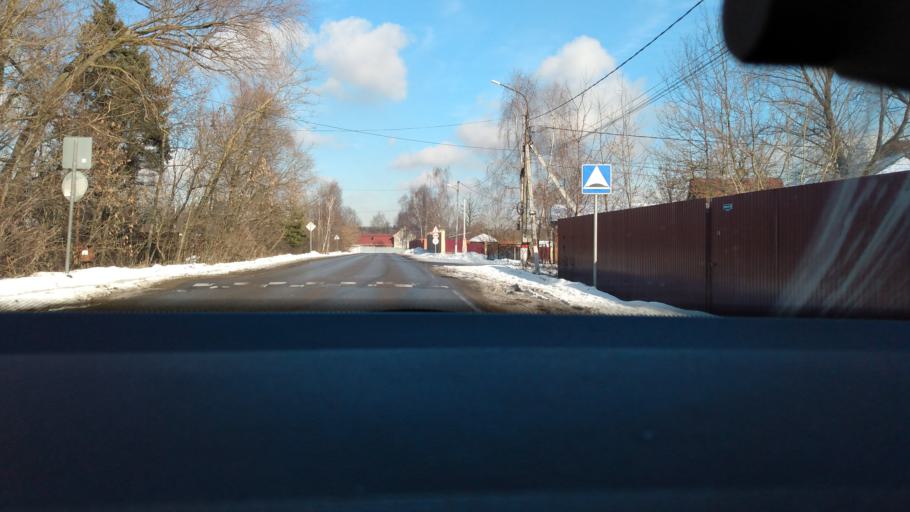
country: RU
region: Moskovskaya
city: Kratovo
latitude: 55.6370
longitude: 38.1650
